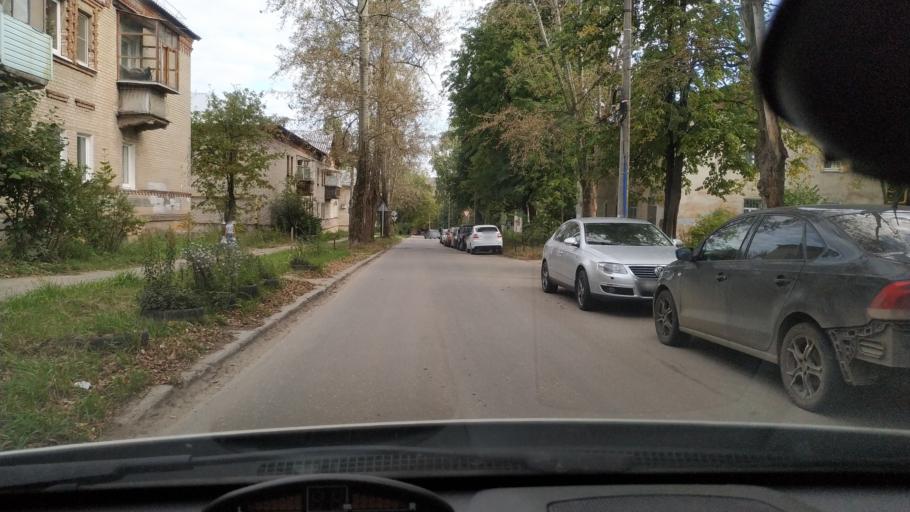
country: RU
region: Rjazan
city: Ryazan'
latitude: 54.6043
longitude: 39.7214
